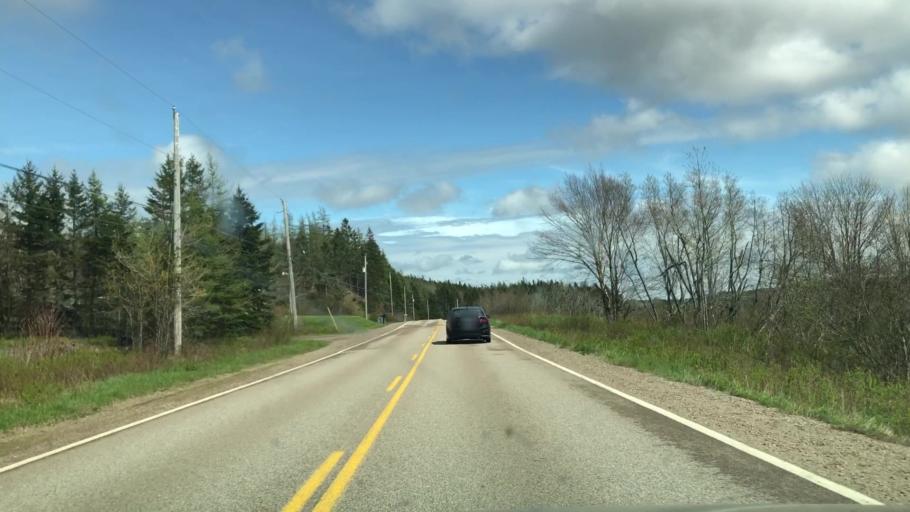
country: CA
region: Nova Scotia
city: Antigonish
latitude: 45.1925
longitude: -61.9939
